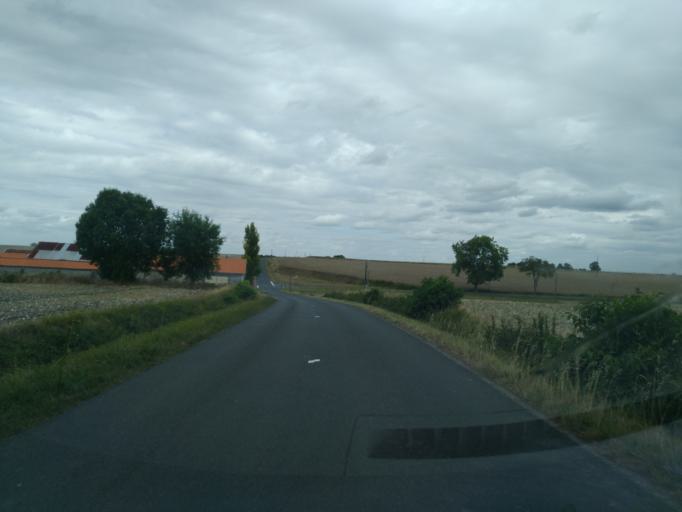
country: FR
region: Poitou-Charentes
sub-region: Departement de la Charente-Maritime
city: Perignac
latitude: 45.6471
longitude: -0.5258
